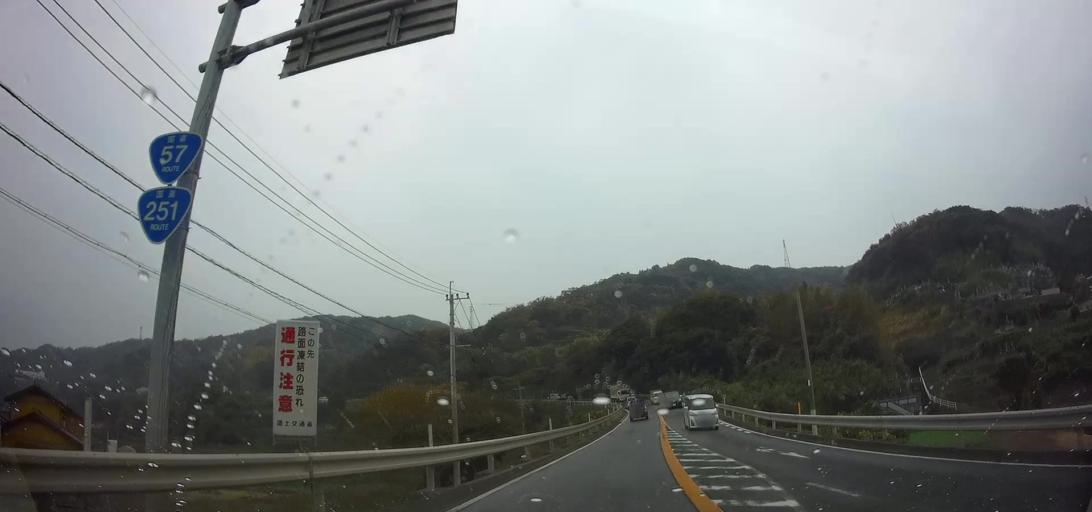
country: JP
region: Nagasaki
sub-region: Isahaya-shi
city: Isahaya
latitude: 32.7935
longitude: 130.1833
